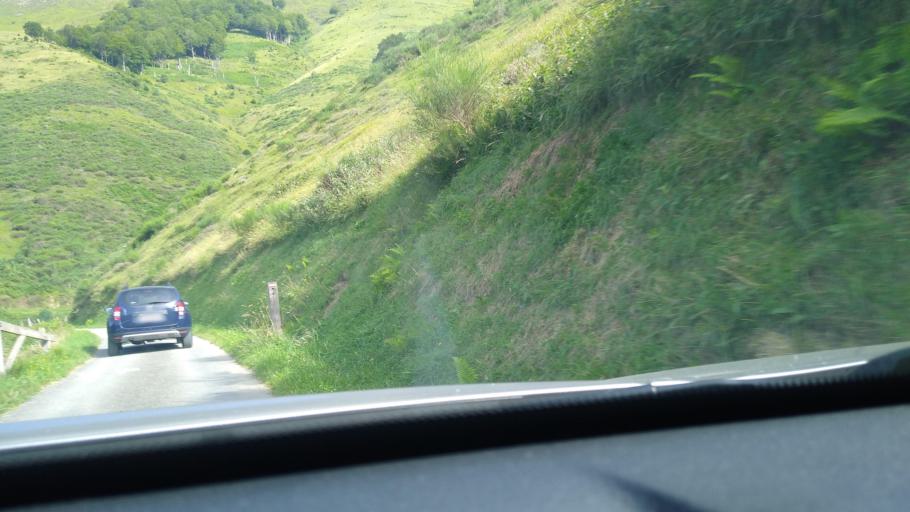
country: FR
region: Midi-Pyrenees
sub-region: Departement de l'Ariege
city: Saint-Girons
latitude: 42.7921
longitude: 1.1615
